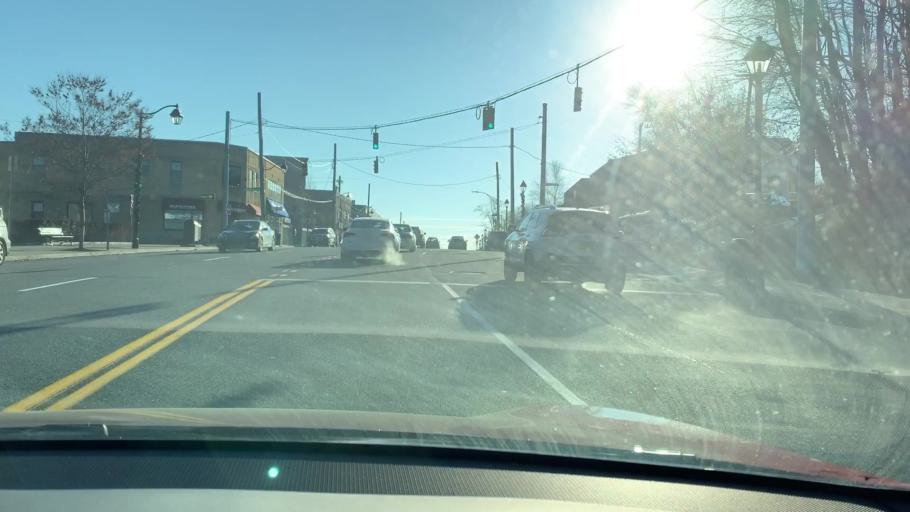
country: US
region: New York
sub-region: Westchester County
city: Elmsford
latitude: 41.0540
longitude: -73.8171
